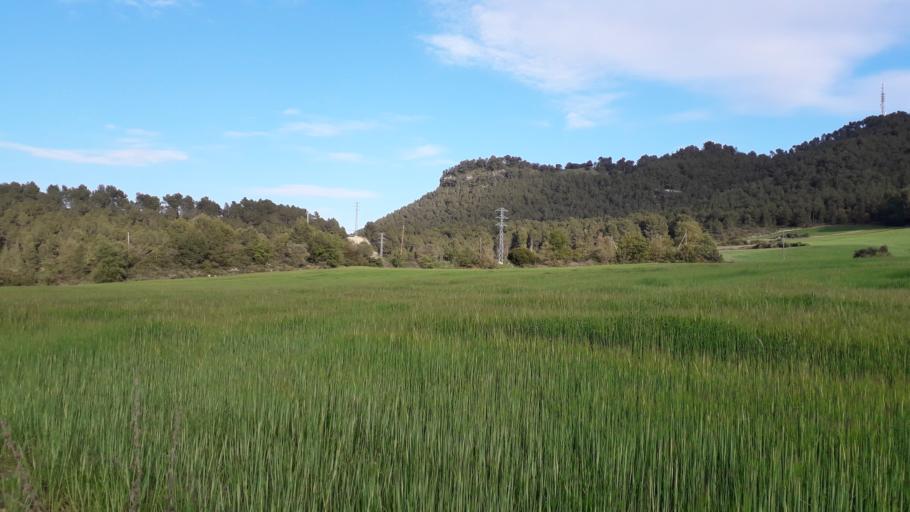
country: ES
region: Catalonia
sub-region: Provincia de Barcelona
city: Orpi
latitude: 41.5595
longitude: 1.5718
